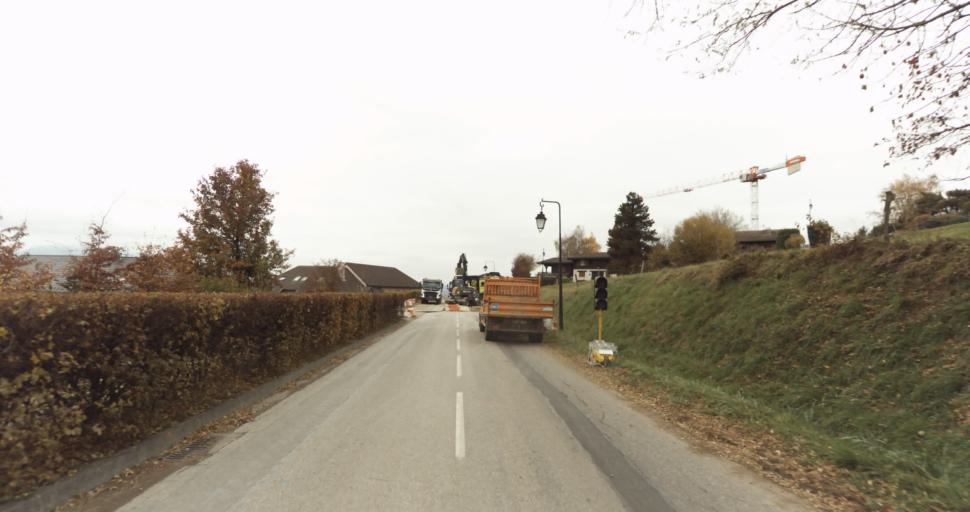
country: FR
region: Rhone-Alpes
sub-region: Departement de la Haute-Savoie
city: Saint-Martin-Bellevue
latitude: 45.9460
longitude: 6.1463
